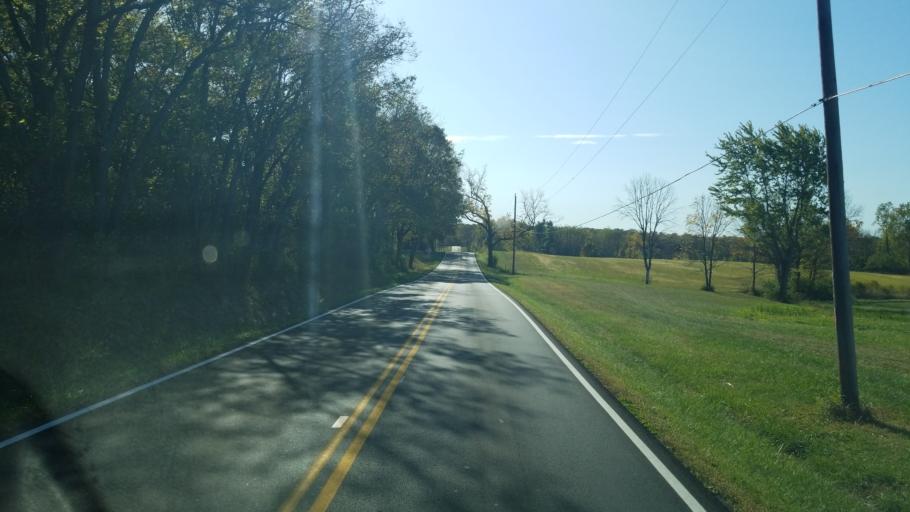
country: US
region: Ohio
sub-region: Warren County
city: Morrow
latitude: 39.3924
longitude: -84.0724
